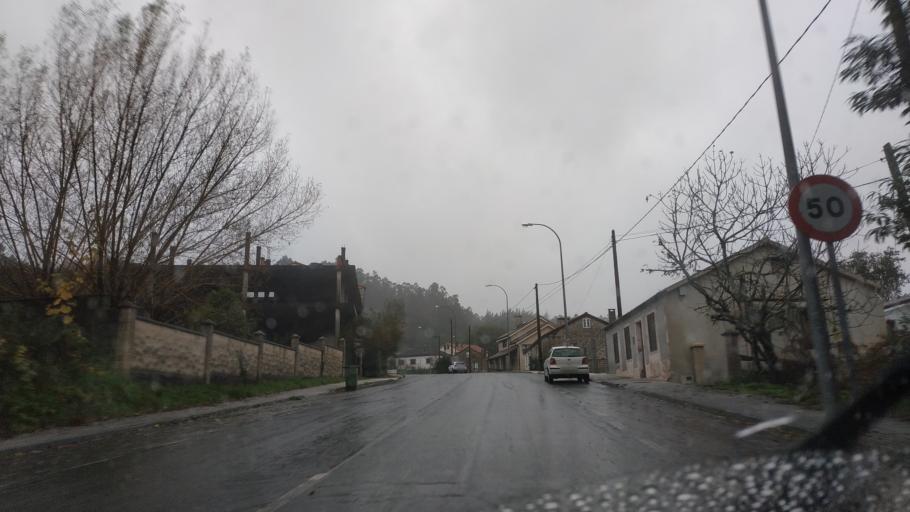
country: ES
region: Galicia
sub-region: Provincia da Coruna
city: Negreira
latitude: 42.9064
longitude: -8.7412
